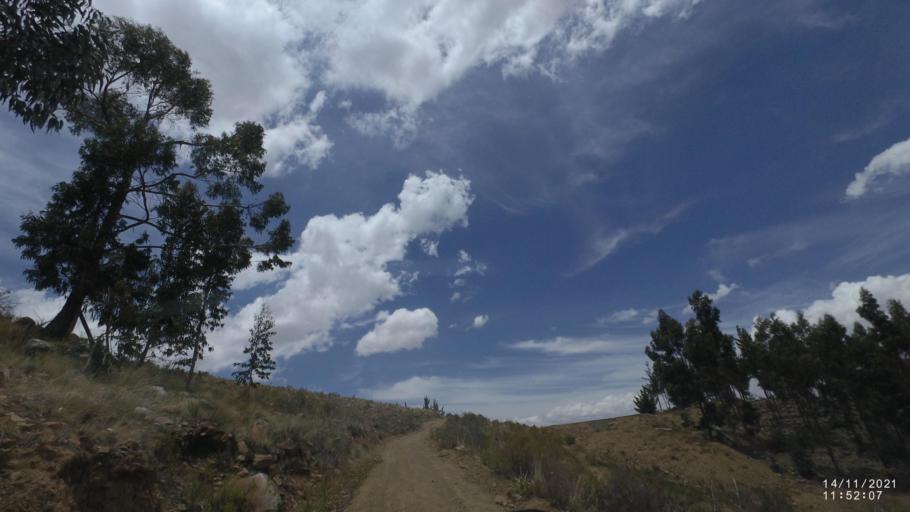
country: BO
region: Cochabamba
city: Colomi
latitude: -17.3622
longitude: -65.9828
